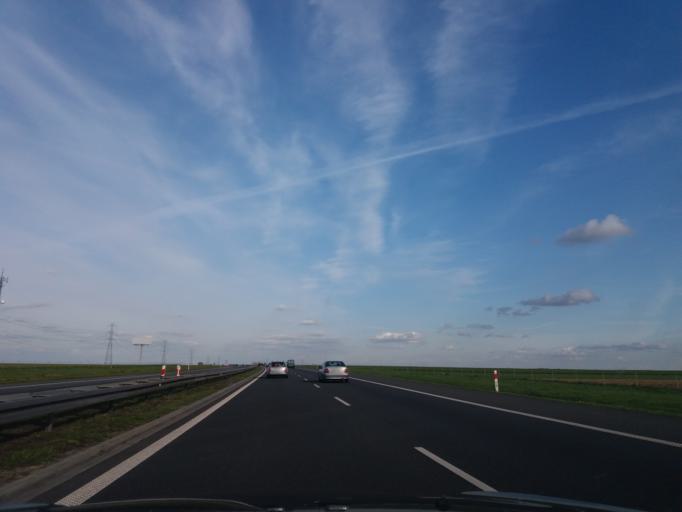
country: PL
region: Opole Voivodeship
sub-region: Powiat brzeski
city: Olszanka
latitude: 50.7380
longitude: 17.4724
